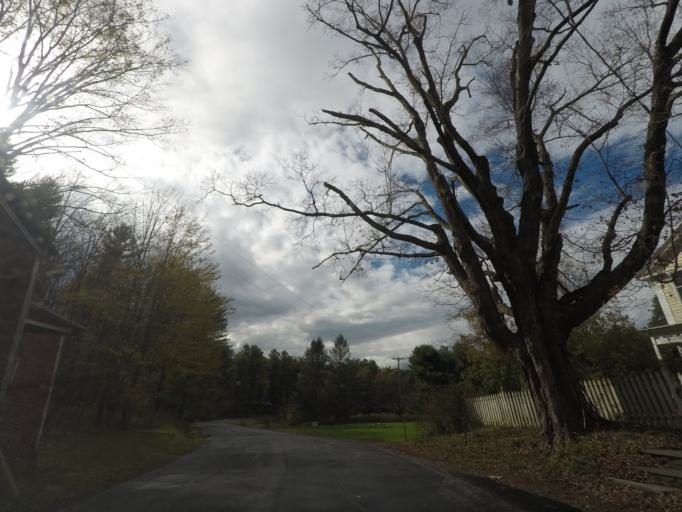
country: US
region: New York
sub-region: Rensselaer County
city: East Greenbush
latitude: 42.5799
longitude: -73.6433
